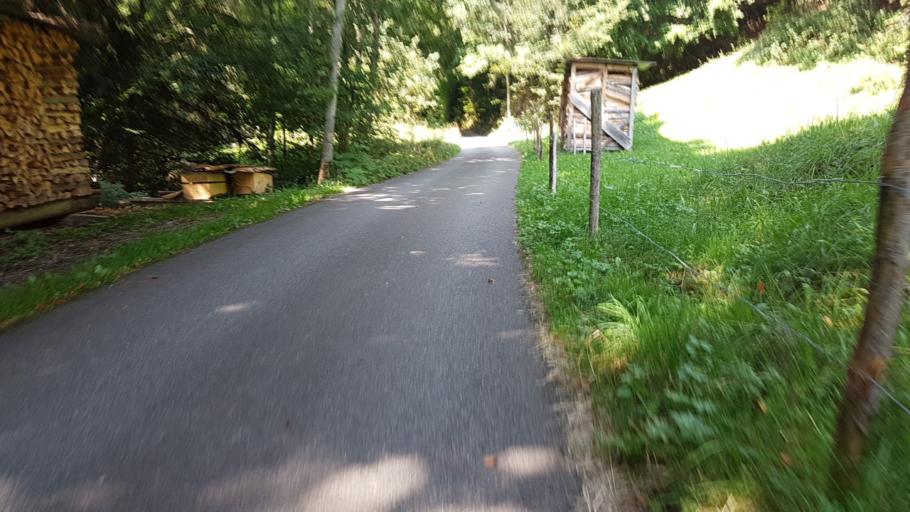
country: CH
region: Bern
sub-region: Frutigen-Niedersimmental District
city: Aeschi
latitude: 46.5976
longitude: 7.7165
